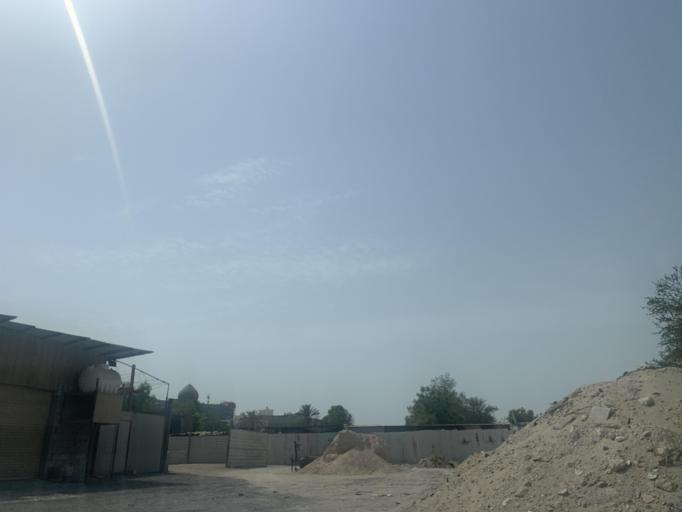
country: BH
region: Manama
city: Jidd Hafs
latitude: 26.2110
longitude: 50.4634
